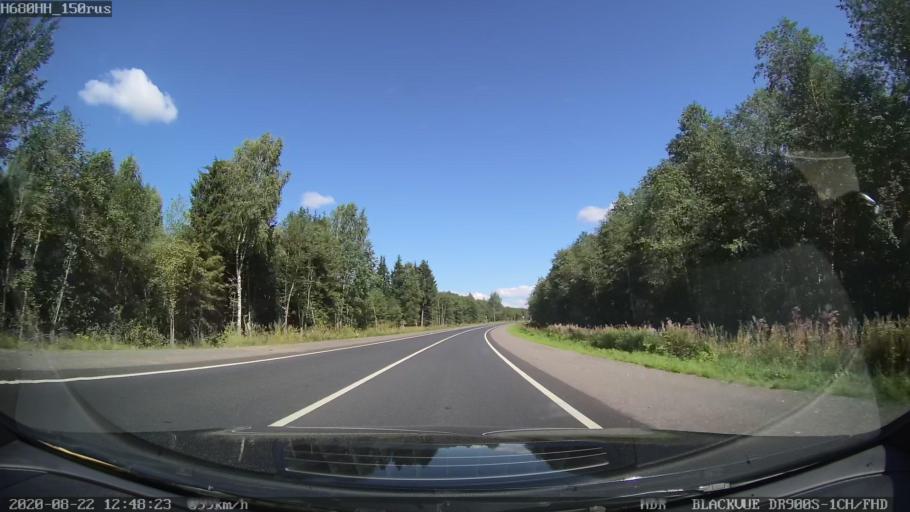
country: RU
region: Tverskaya
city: Rameshki
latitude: 57.4391
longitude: 36.1839
